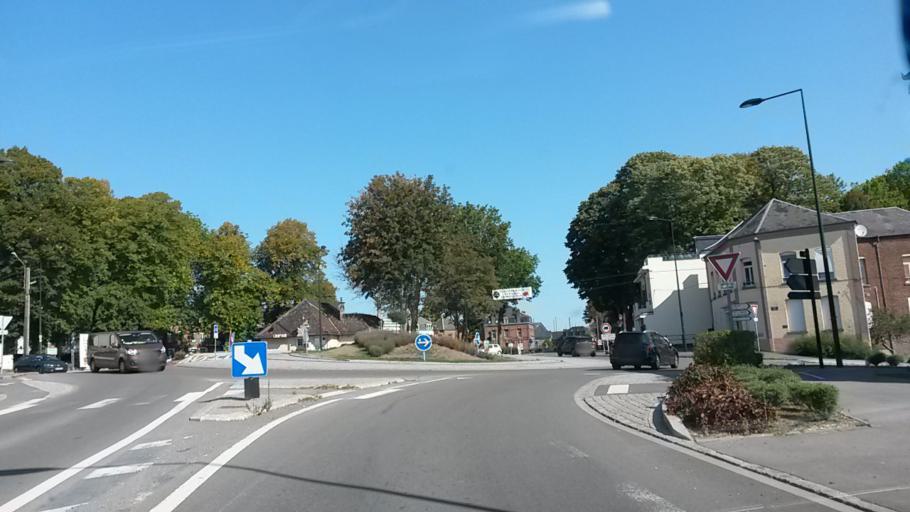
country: FR
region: Nord-Pas-de-Calais
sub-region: Departement du Nord
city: Avesnes-sur-Helpe
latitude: 50.1183
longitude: 3.9322
